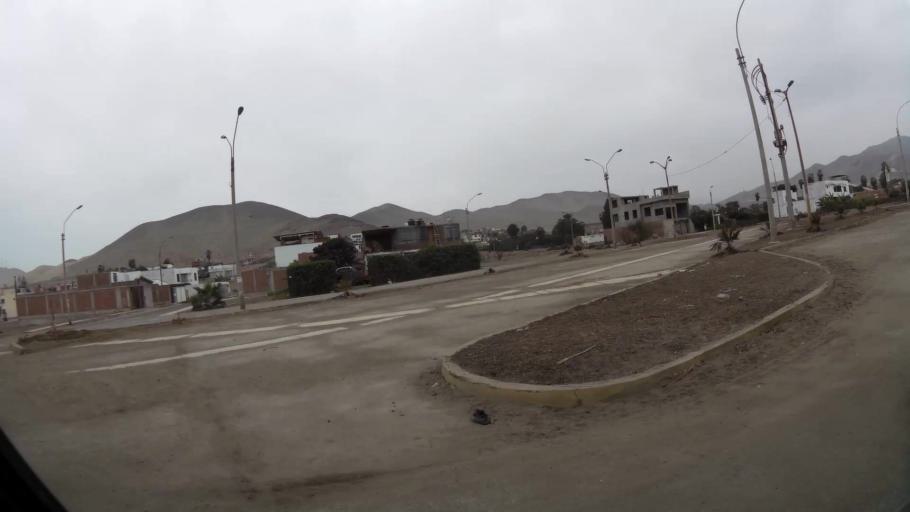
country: PE
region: Lima
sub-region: Lima
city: Santa Rosa
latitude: -11.7974
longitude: -77.1749
